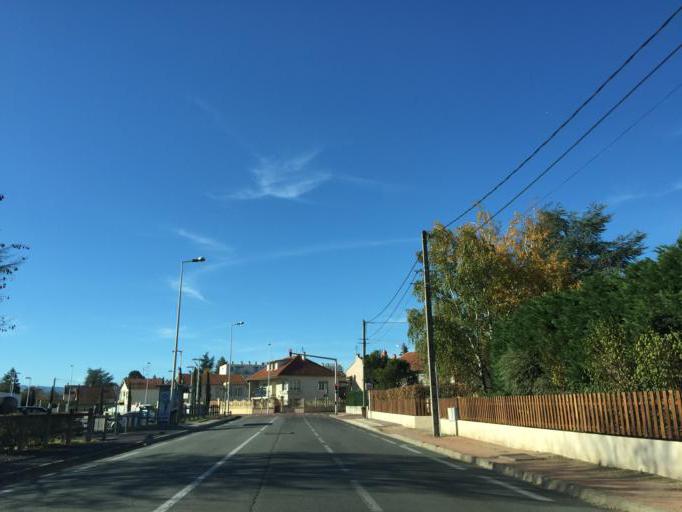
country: FR
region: Rhone-Alpes
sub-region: Departement de la Loire
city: Riorges
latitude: 46.0341
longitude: 4.0533
